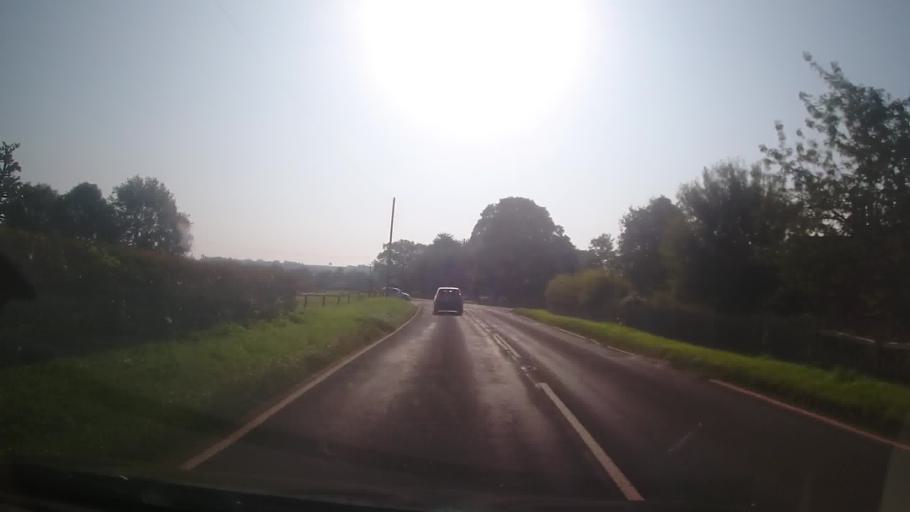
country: GB
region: England
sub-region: Shropshire
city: Alveley
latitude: 52.4961
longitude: -2.3679
